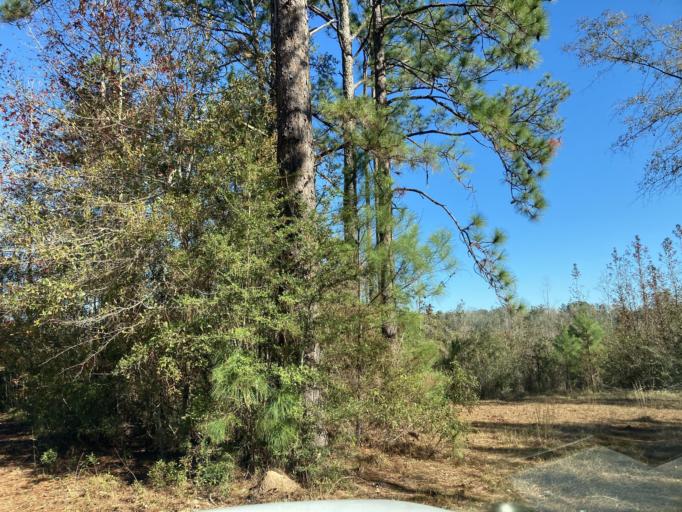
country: US
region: Mississippi
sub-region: Lamar County
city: Sumrall
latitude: 31.2917
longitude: -89.6034
